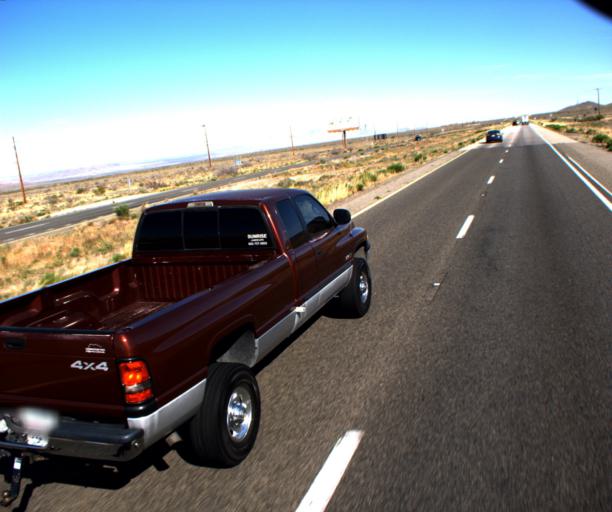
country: US
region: Arizona
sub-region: Mohave County
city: Golden Valley
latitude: 35.3981
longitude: -114.2600
